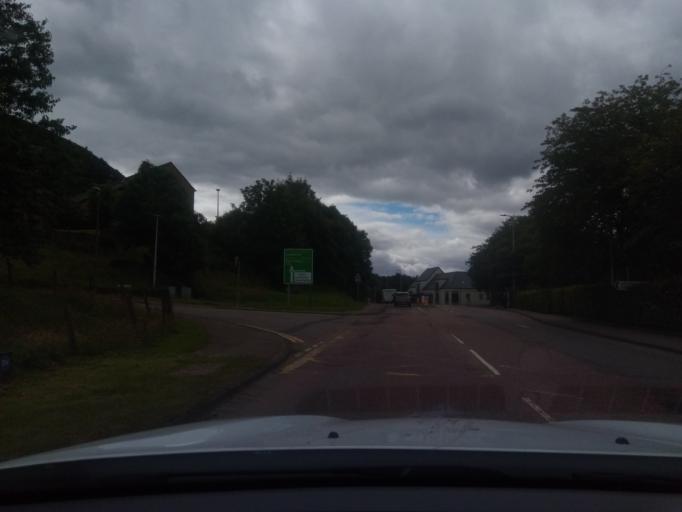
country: GB
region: Scotland
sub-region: Highland
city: Fort William
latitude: 56.8233
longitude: -5.0909
